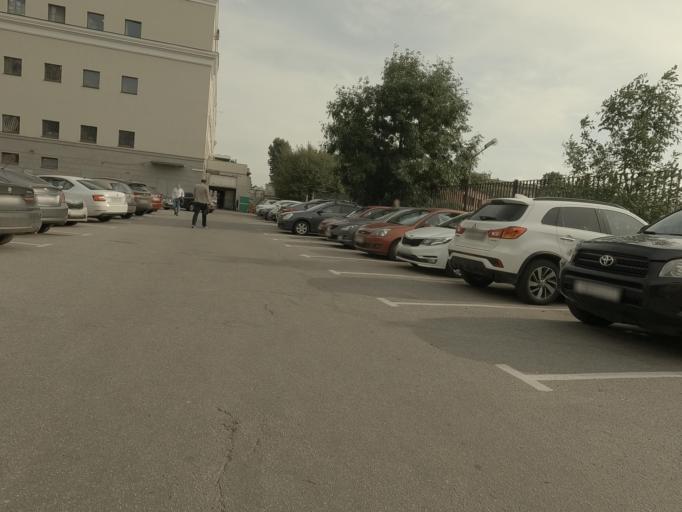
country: RU
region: St.-Petersburg
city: Admiralteisky
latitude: 59.9012
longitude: 30.2708
